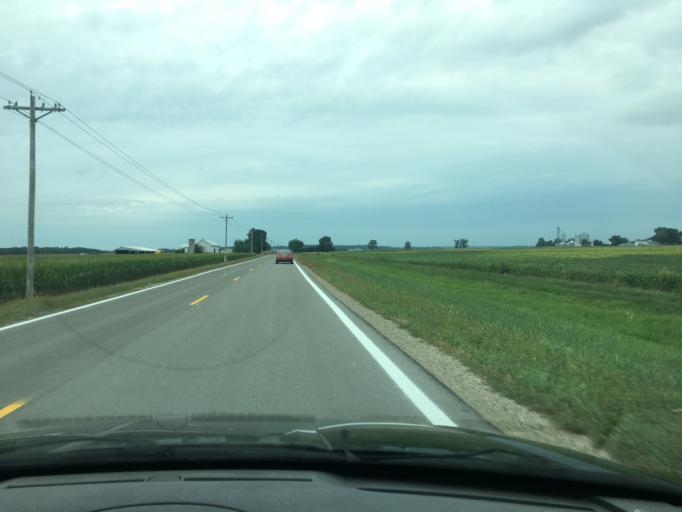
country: US
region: Ohio
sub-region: Logan County
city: West Liberty
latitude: 40.1870
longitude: -83.7818
